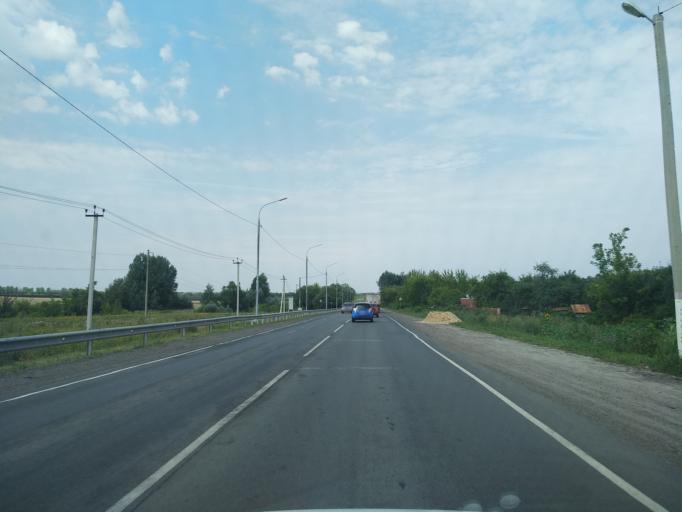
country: RU
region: Voronezj
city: Orlovo
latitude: 51.6797
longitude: 39.6474
